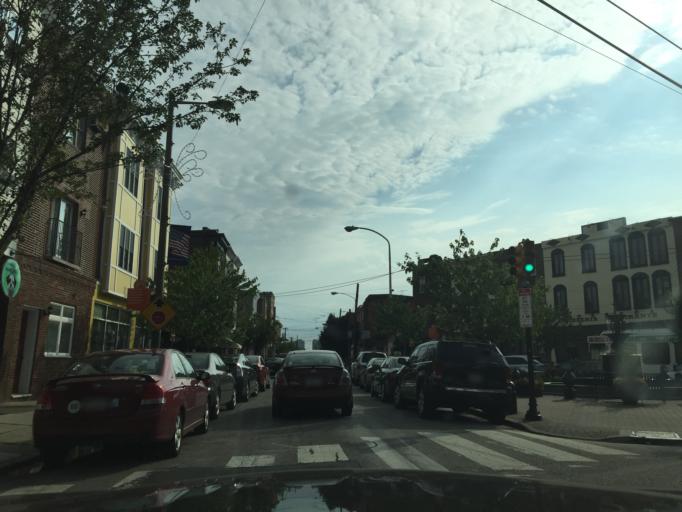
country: US
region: Pennsylvania
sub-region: Philadelphia County
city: Philadelphia
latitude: 39.9299
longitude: -75.1635
